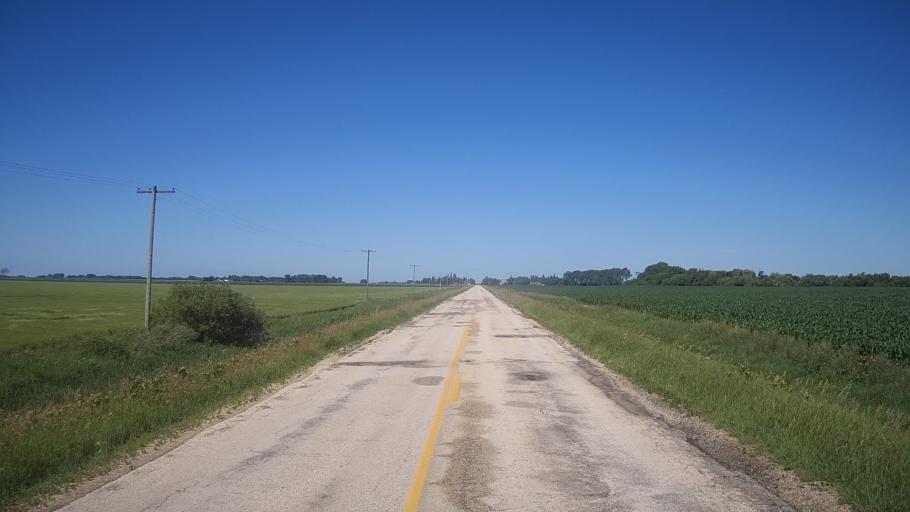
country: CA
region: Manitoba
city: Portage la Prairie
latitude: 50.0435
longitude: -98.0377
